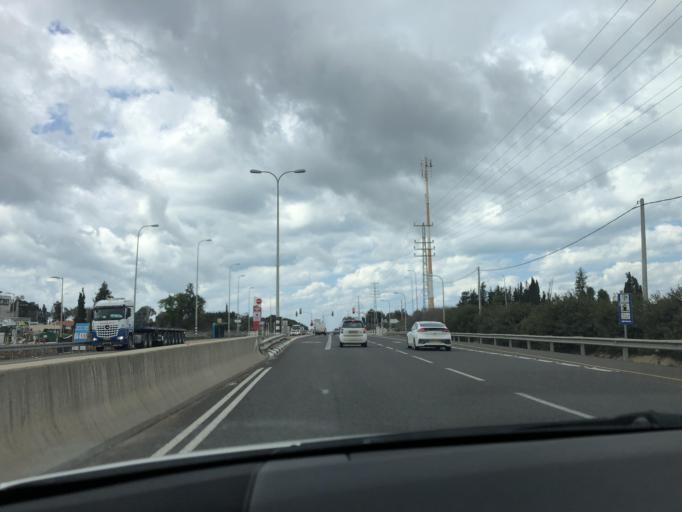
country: IL
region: Central District
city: Even Yehuda
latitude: 32.2556
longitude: 34.8754
